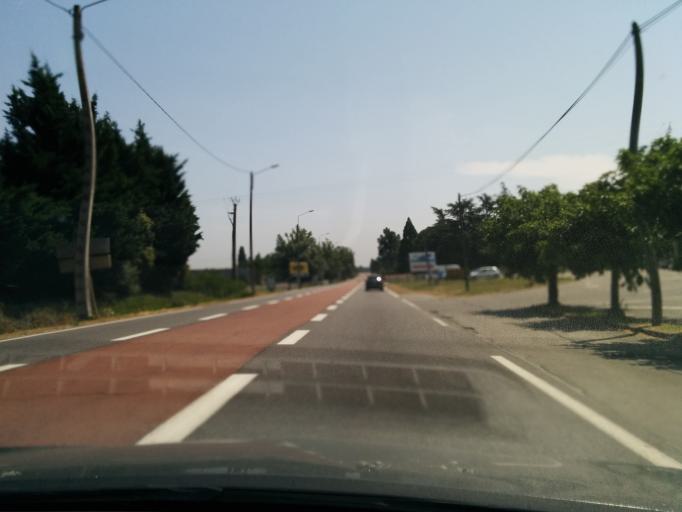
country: FR
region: Midi-Pyrenees
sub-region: Departement de la Haute-Garonne
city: Pompertuzat
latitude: 43.4929
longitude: 1.5229
